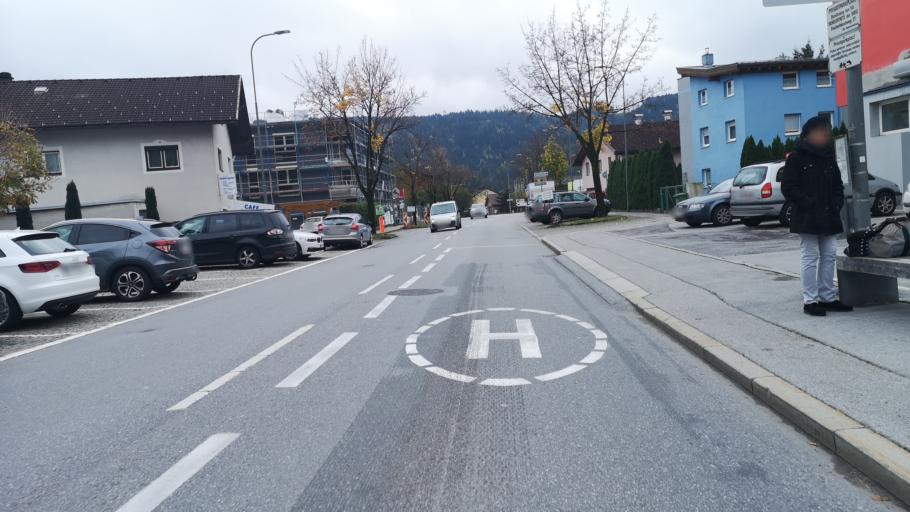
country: AT
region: Tyrol
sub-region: Politischer Bezirk Innsbruck Land
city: Natters
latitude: 47.2617
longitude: 11.3652
